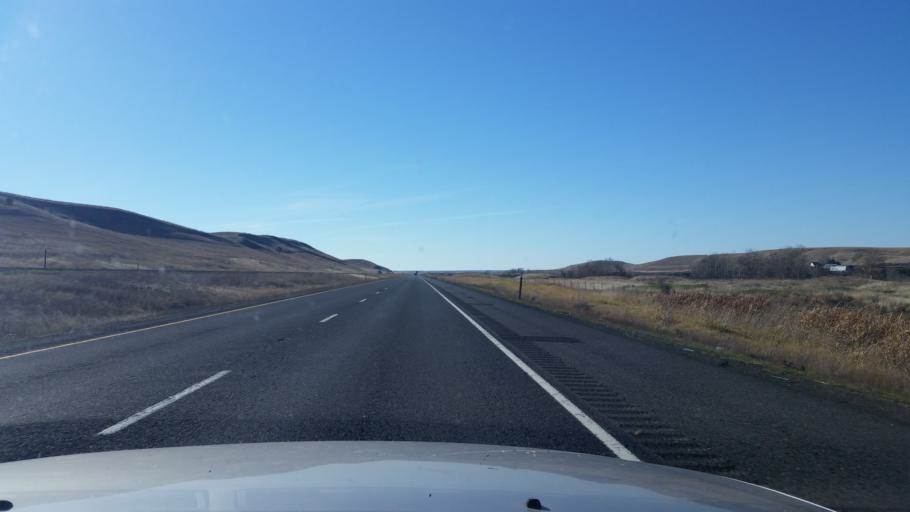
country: US
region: Washington
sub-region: Spokane County
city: Medical Lake
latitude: 47.3611
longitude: -117.8889
